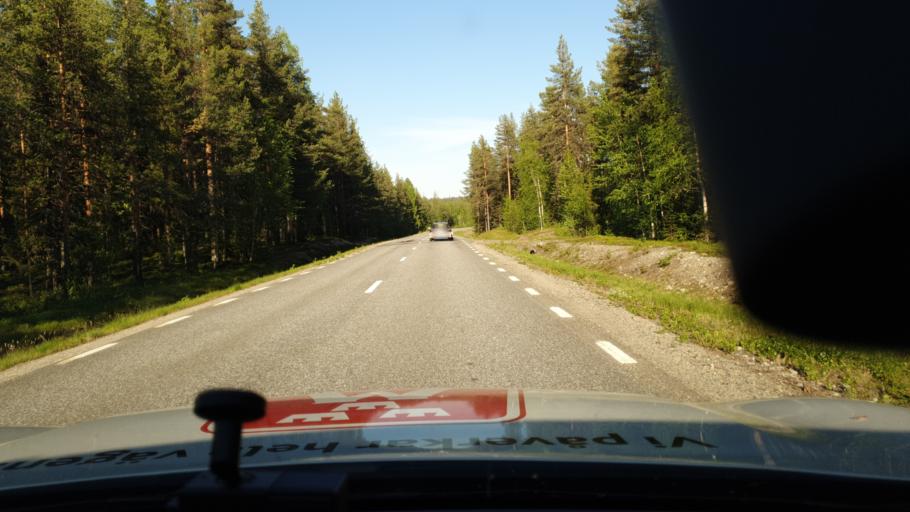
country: SE
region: Vaesterbotten
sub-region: Lycksele Kommun
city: Soderfors
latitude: 64.6209
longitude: 18.2920
